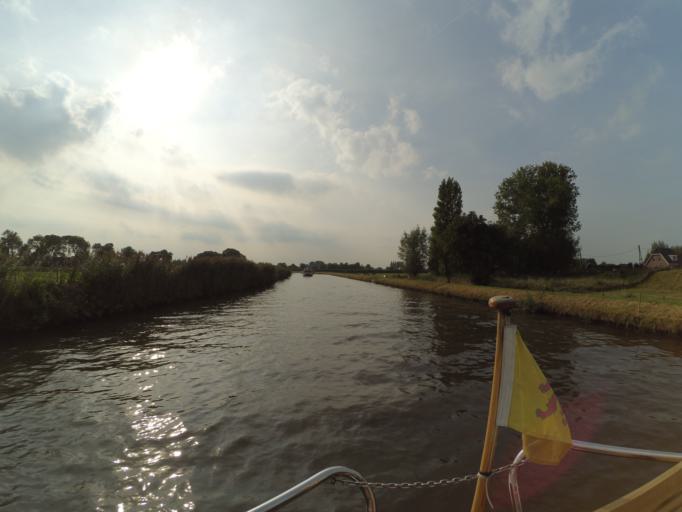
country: NL
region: Utrecht
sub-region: Gemeente IJsselstein
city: IJsselstein
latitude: 52.0534
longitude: 5.0117
